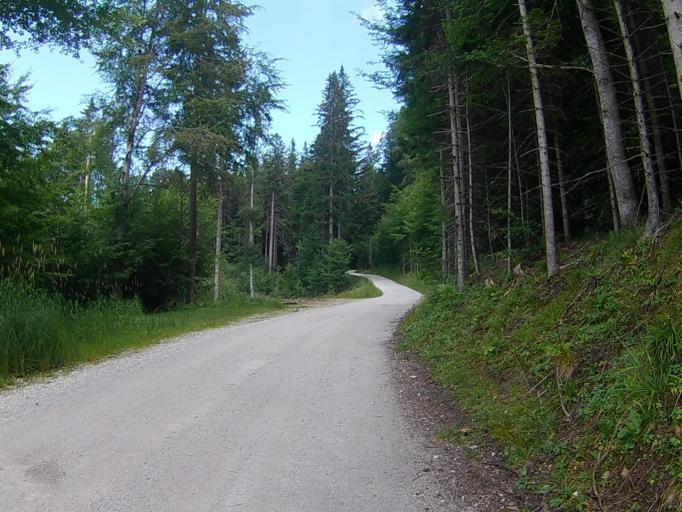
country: SI
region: Selnica ob Dravi
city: Selnica ob Dravi
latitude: 46.4944
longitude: 15.4661
